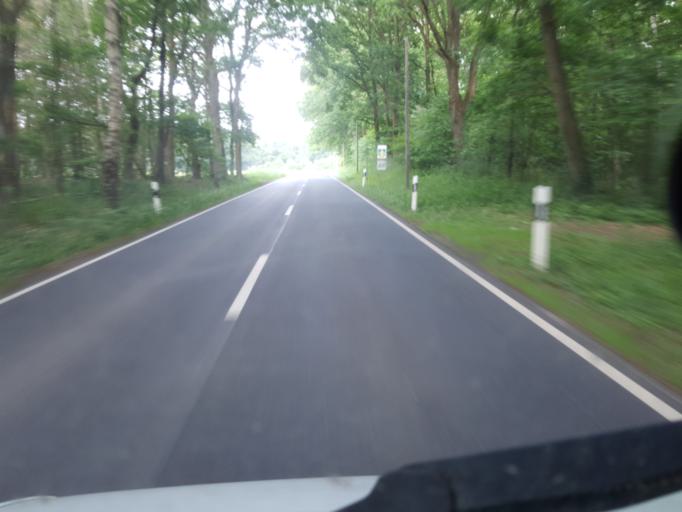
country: DE
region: Lower Saxony
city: Liebenau
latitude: 52.5867
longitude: 9.0763
